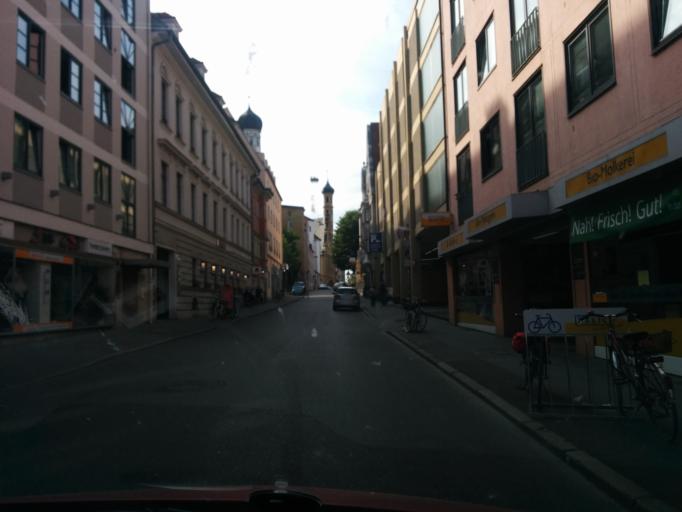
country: DE
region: Bavaria
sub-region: Swabia
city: Augsburg
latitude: 48.3704
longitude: 10.8938
